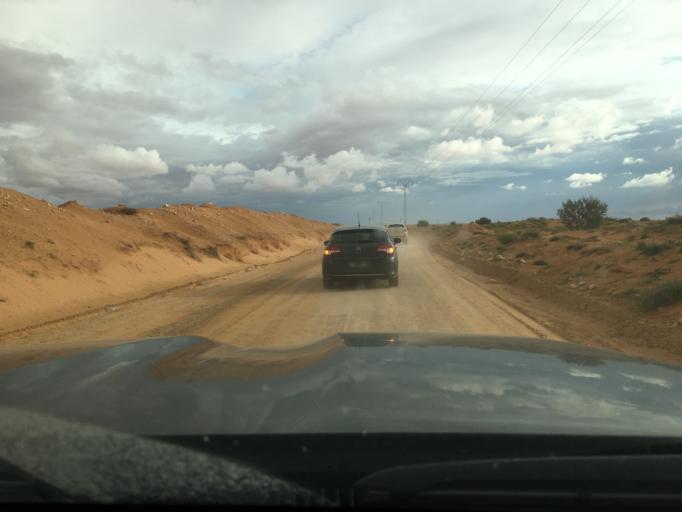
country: TN
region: Madanin
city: Medenine
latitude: 33.2723
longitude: 10.5661
